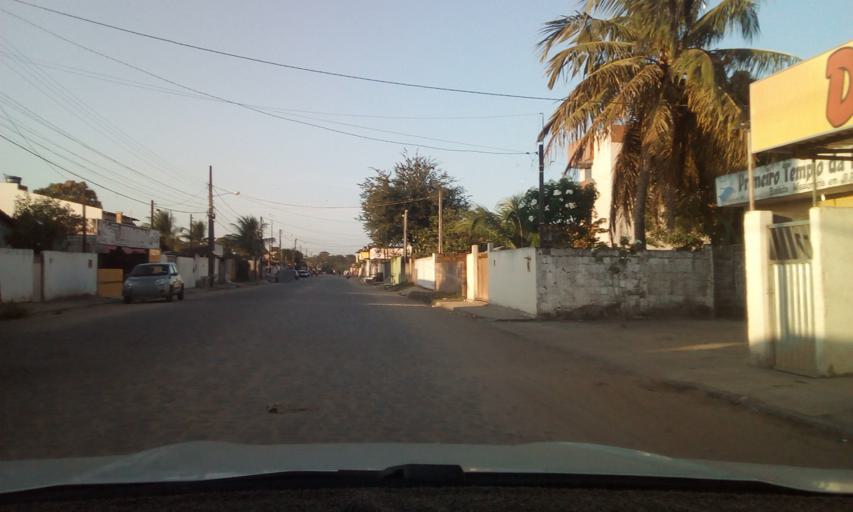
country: BR
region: Paraiba
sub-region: Bayeux
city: Bayeux
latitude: -7.1756
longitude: -34.9305
